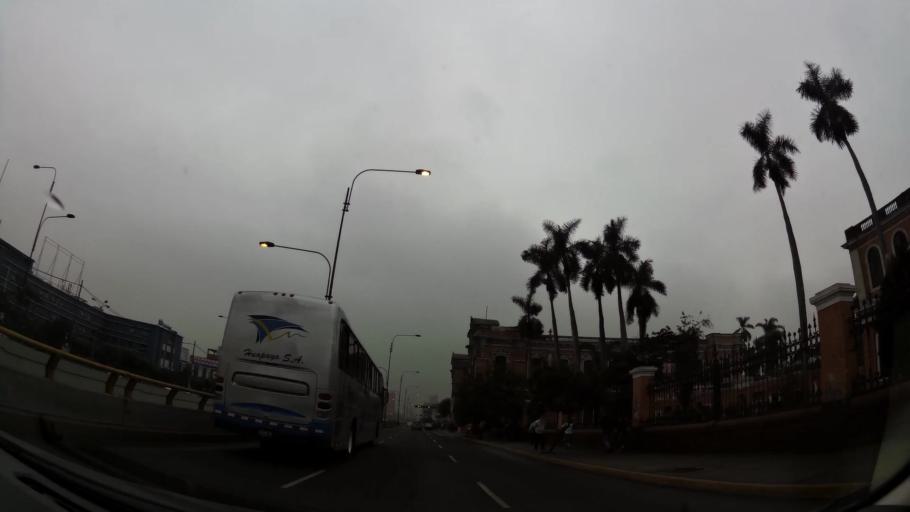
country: PE
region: Lima
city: Lima
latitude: -12.0580
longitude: -77.0223
